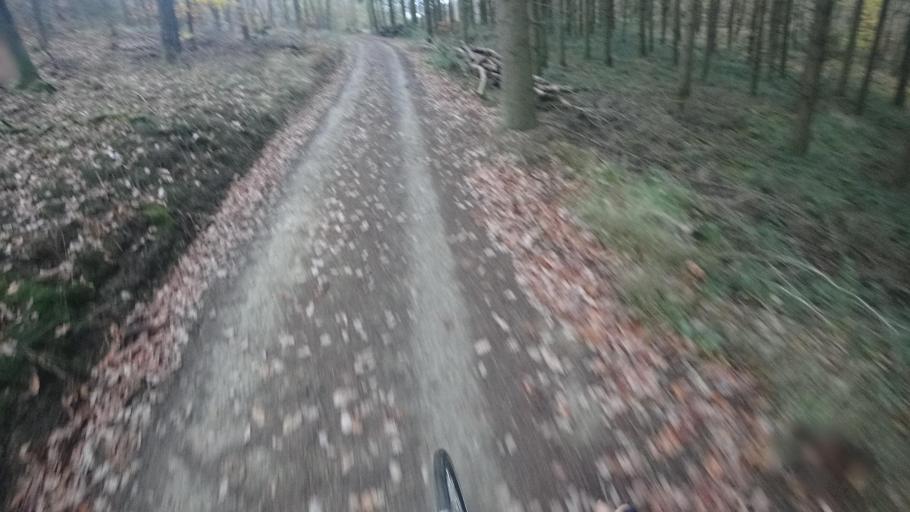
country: DE
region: Rheinland-Pfalz
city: Rech
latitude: 50.5089
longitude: 7.0543
